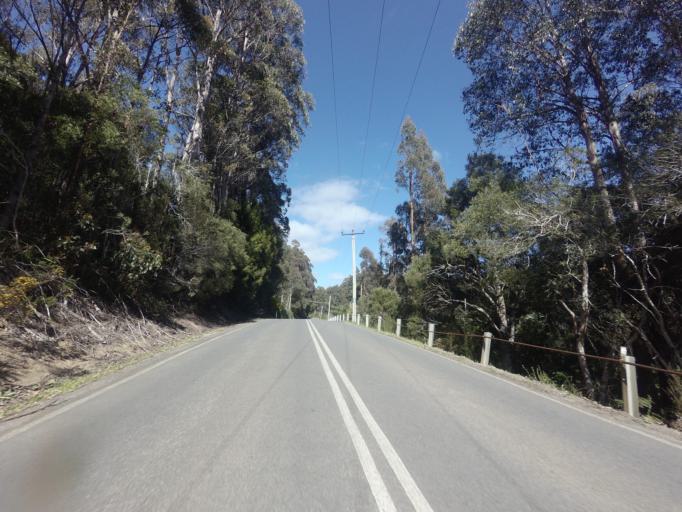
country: AU
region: Tasmania
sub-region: Derwent Valley
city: New Norfolk
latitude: -42.7132
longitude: 146.6964
